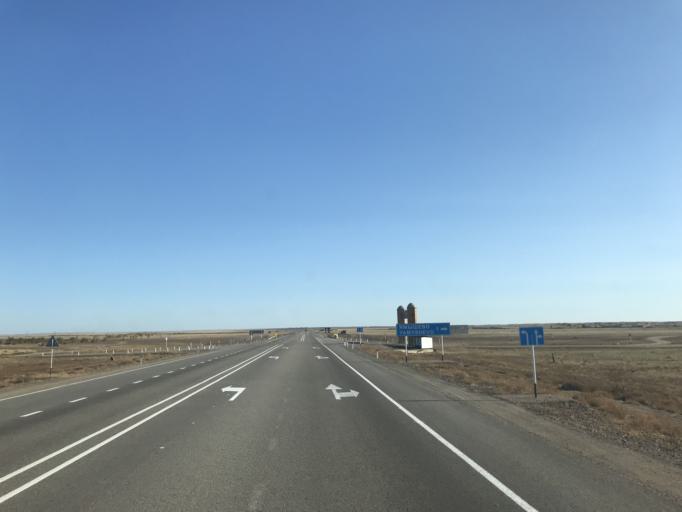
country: KZ
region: Pavlodar
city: Koktobe
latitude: 51.8979
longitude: 77.3908
